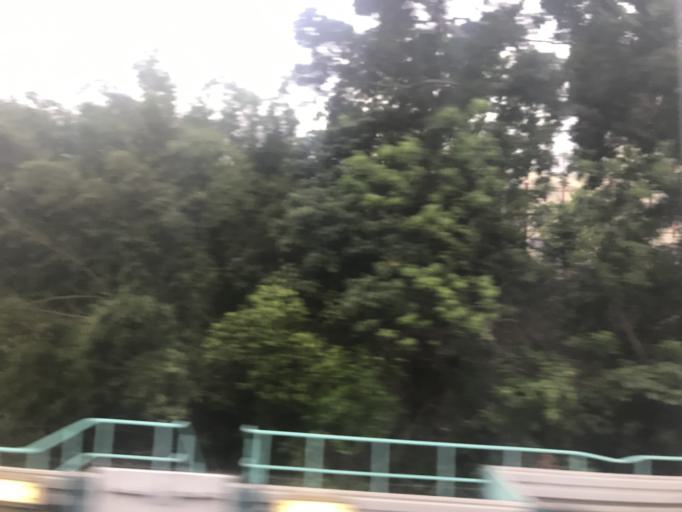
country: HK
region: Kowloon City
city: Kowloon
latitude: 22.3287
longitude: 114.1755
